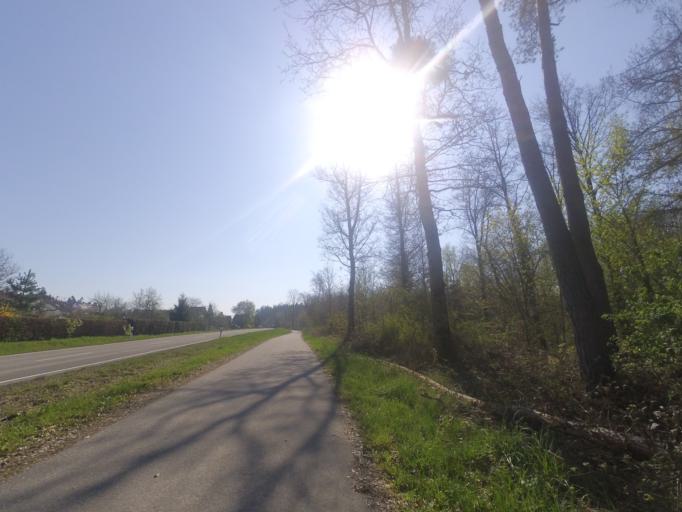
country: DE
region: Bavaria
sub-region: Swabia
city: Nersingen
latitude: 48.4121
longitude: 10.1469
